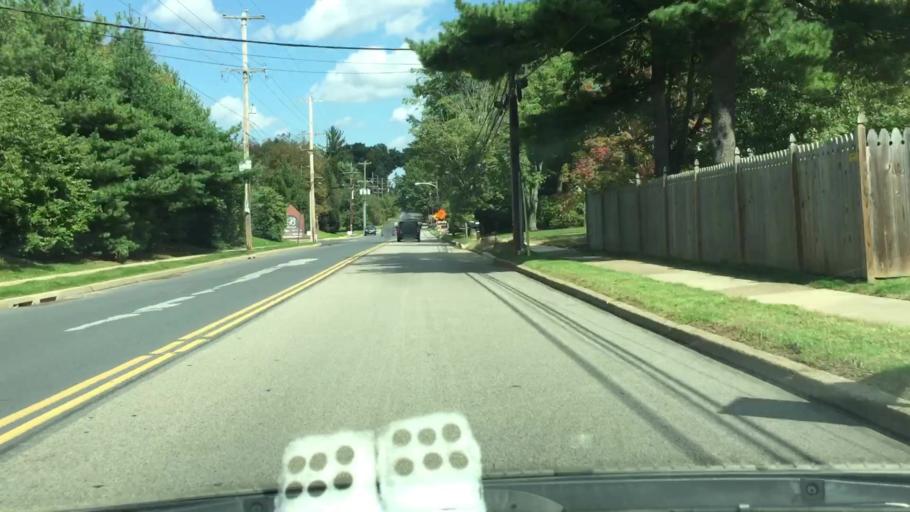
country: US
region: Pennsylvania
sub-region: Montgomery County
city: Norristown
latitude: 40.1374
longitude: -75.3039
